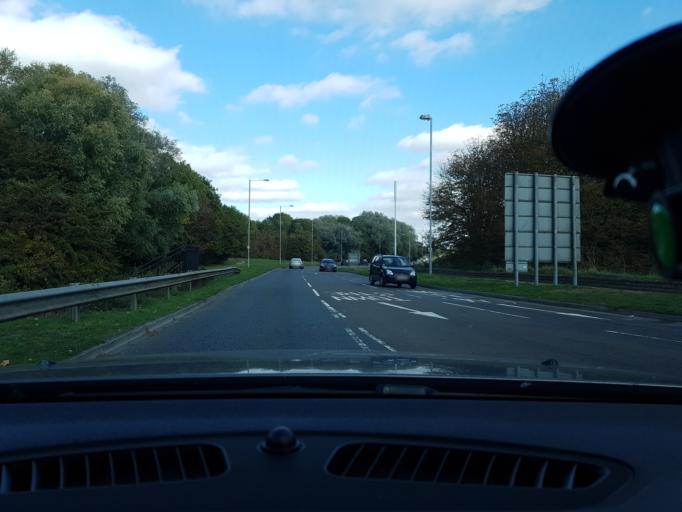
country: GB
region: England
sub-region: Borough of Swindon
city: Chiseldon
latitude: 51.5461
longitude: -1.7450
